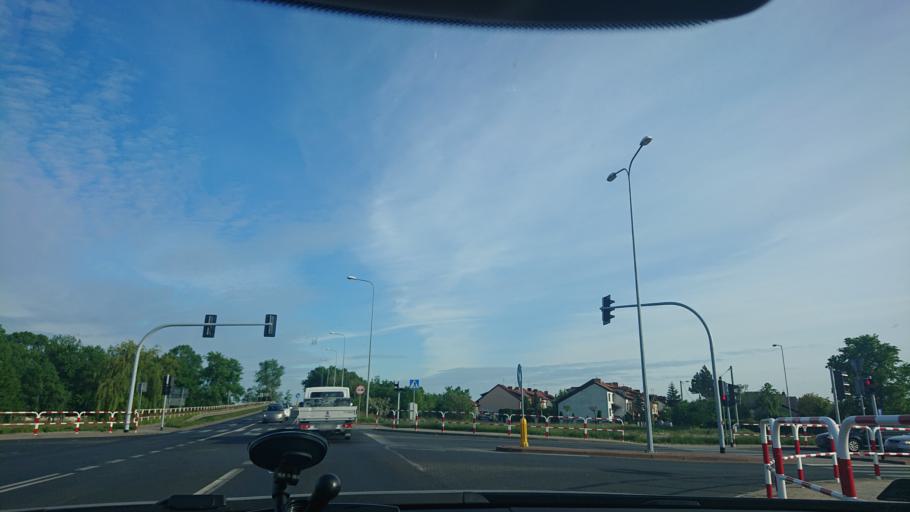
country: PL
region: Greater Poland Voivodeship
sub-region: Powiat gnieznienski
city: Gniezno
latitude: 52.5294
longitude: 17.5833
